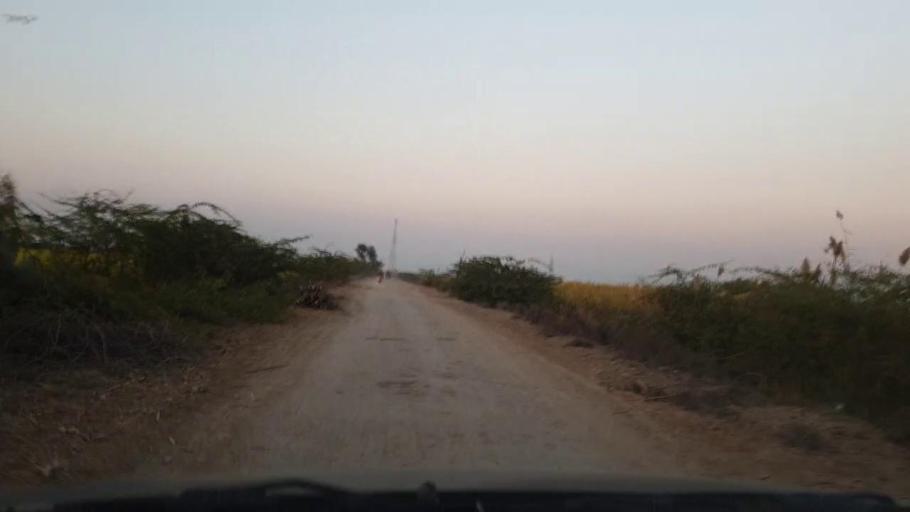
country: PK
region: Sindh
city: Jhol
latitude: 25.9471
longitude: 68.9749
